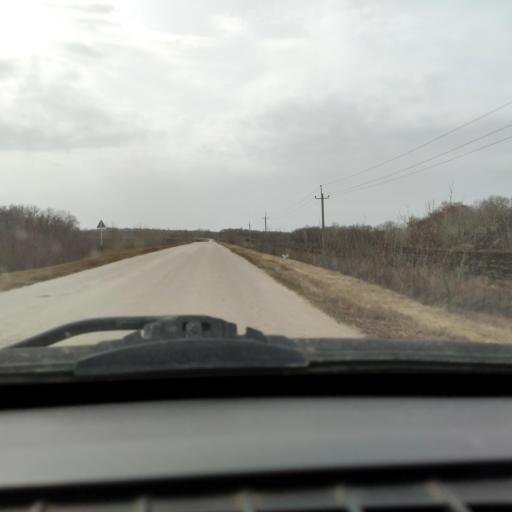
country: RU
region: Samara
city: Dubovyy Umet
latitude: 53.0368
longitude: 50.1691
